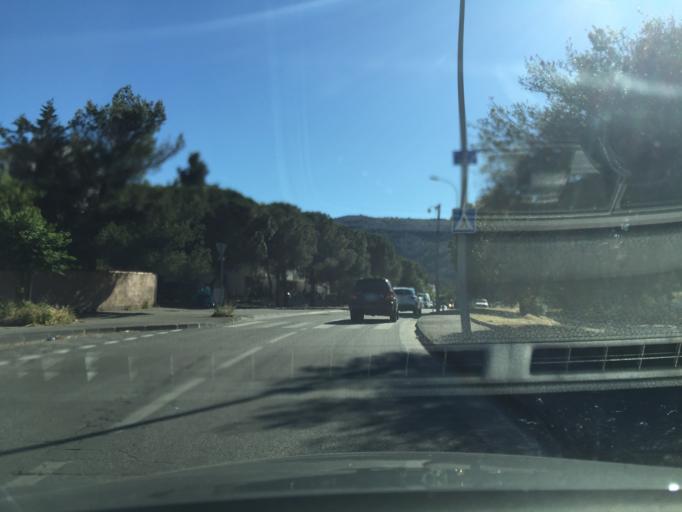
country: FR
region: Provence-Alpes-Cote d'Azur
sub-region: Departement des Bouches-du-Rhone
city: Marseille 09
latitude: 43.2328
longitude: 5.4048
